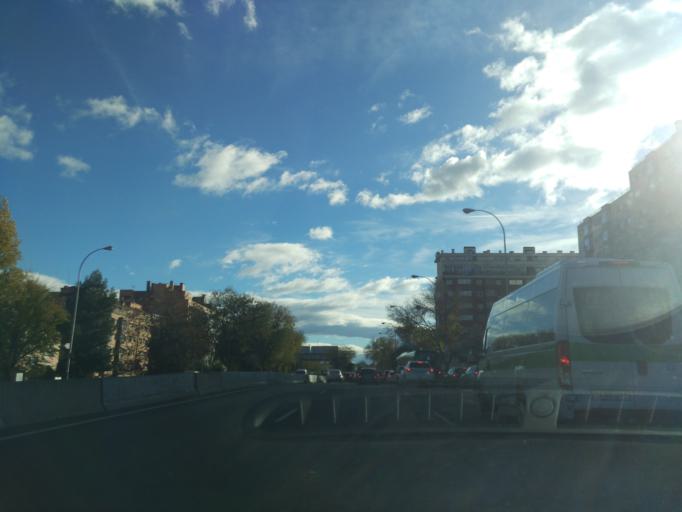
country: ES
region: Madrid
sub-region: Provincia de Madrid
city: Usera
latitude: 40.3738
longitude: -3.6949
